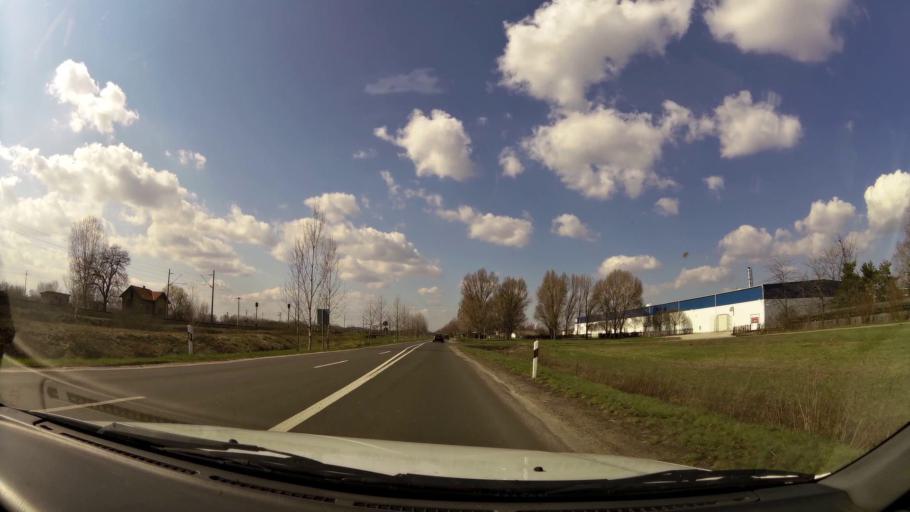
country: HU
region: Pest
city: Nagykata
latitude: 47.3967
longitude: 19.7611
